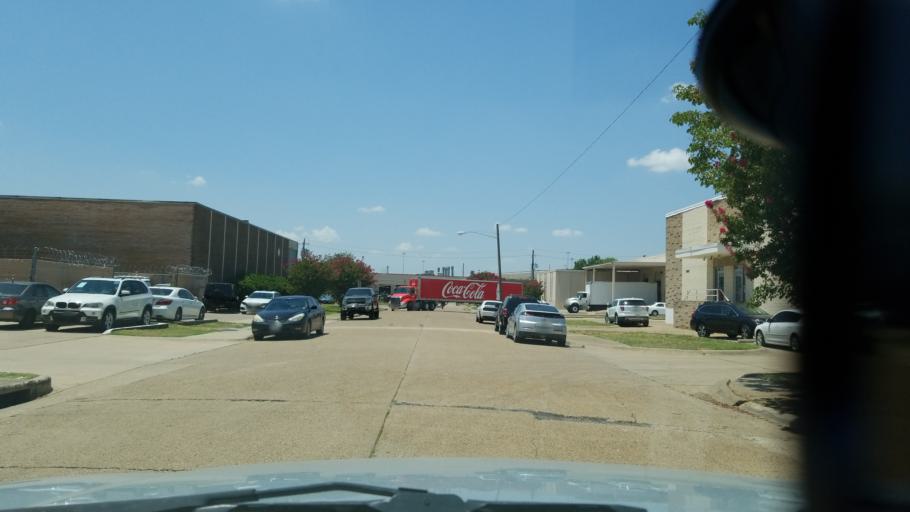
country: US
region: Texas
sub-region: Dallas County
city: Farmers Branch
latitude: 32.9056
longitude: -96.8887
